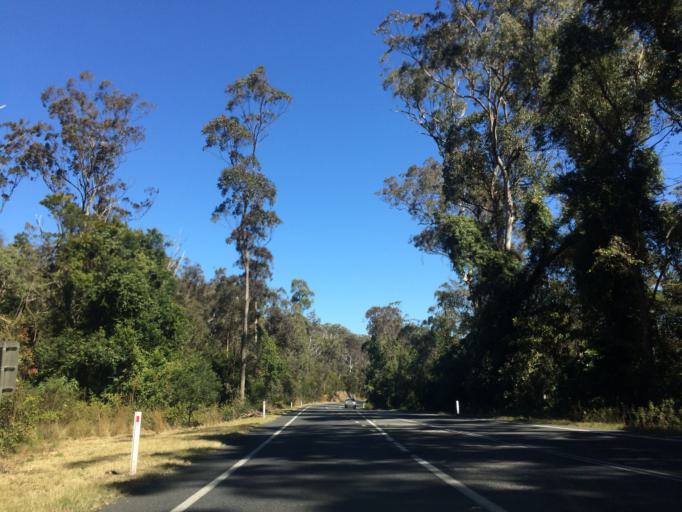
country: AU
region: Queensland
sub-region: Southern Downs
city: Warwick
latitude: -28.0530
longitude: 152.3807
